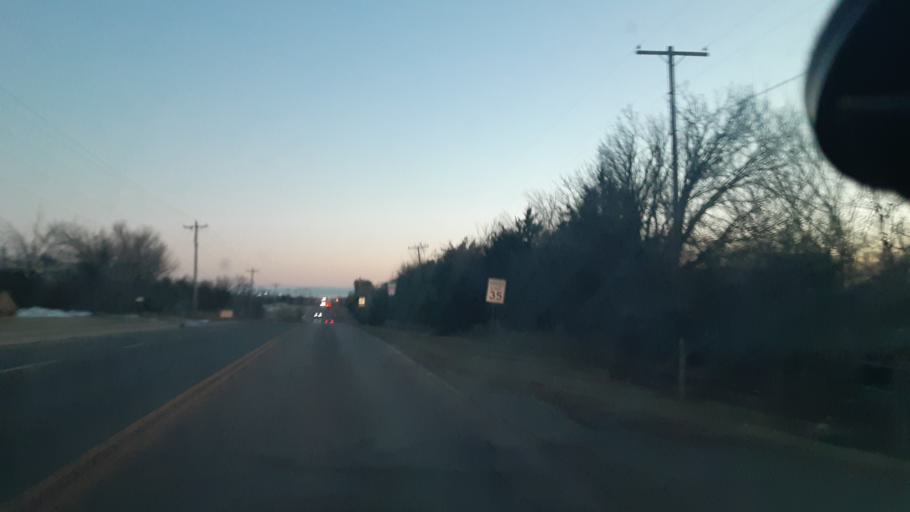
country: US
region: Oklahoma
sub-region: Oklahoma County
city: Edmond
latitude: 35.6668
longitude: -97.4250
